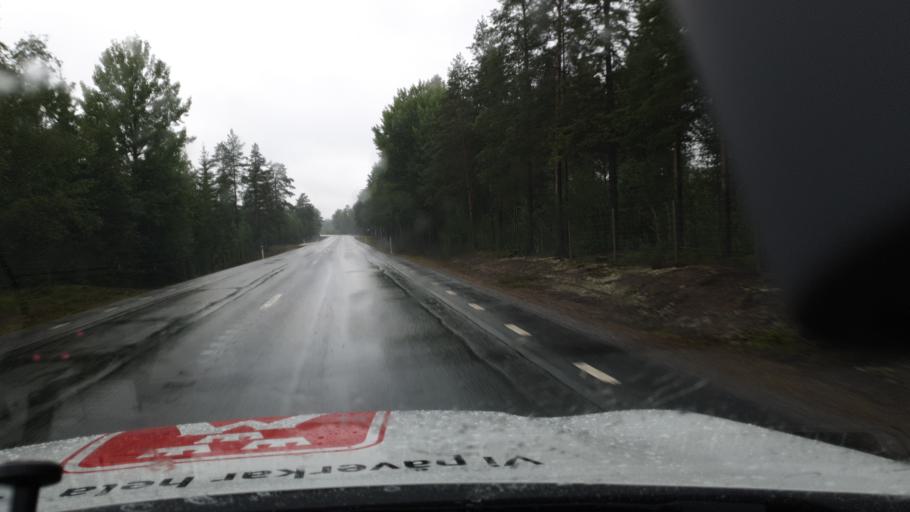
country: SE
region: Vaesterbotten
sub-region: Skelleftea Kommun
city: Burea
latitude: 64.5813
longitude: 21.2208
